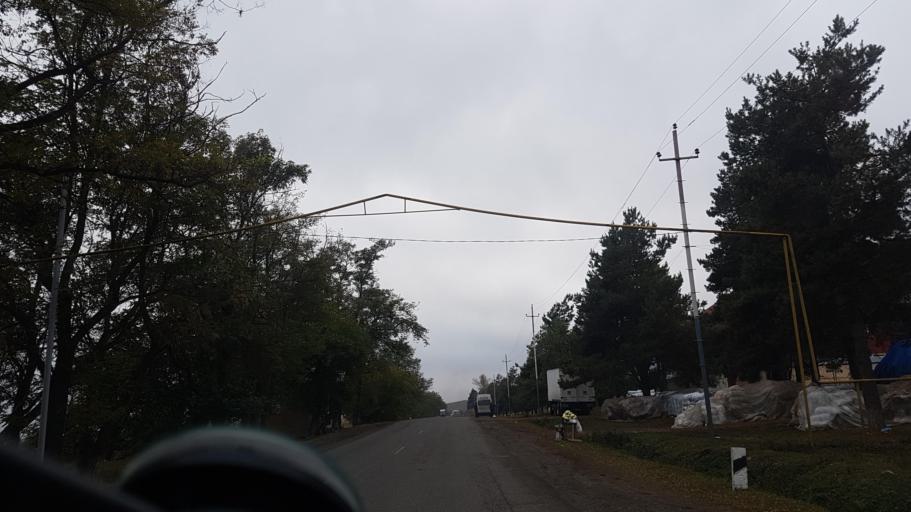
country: AZ
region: Gadabay Rayon
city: Ariqdam
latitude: 40.6427
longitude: 45.8128
